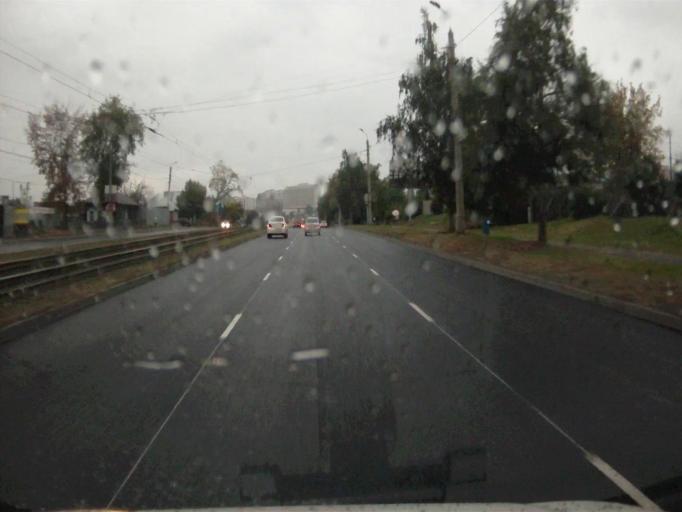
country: RU
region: Chelyabinsk
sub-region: Gorod Chelyabinsk
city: Chelyabinsk
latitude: 55.1855
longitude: 61.3670
